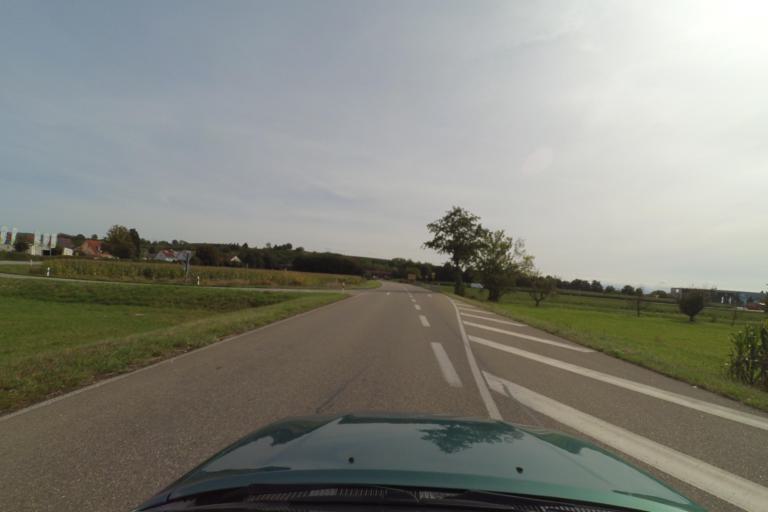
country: DE
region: Baden-Wuerttemberg
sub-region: Freiburg Region
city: Malterdingen
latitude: 48.1583
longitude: 7.7795
